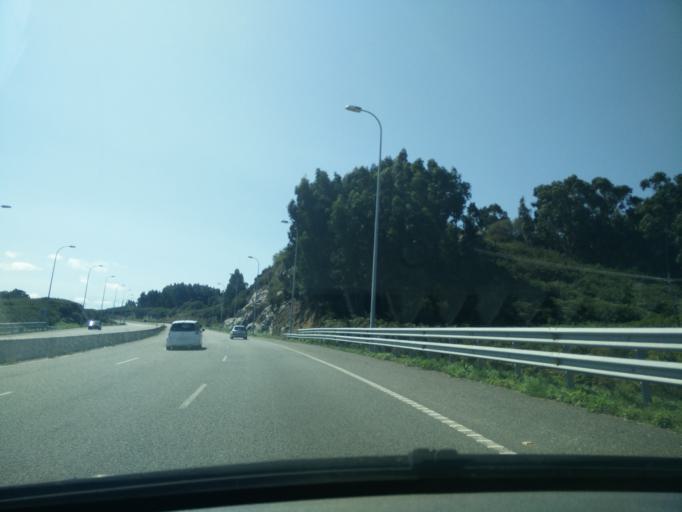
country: ES
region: Galicia
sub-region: Provincia da Coruna
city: A Coruna
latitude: 43.3652
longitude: -8.4319
